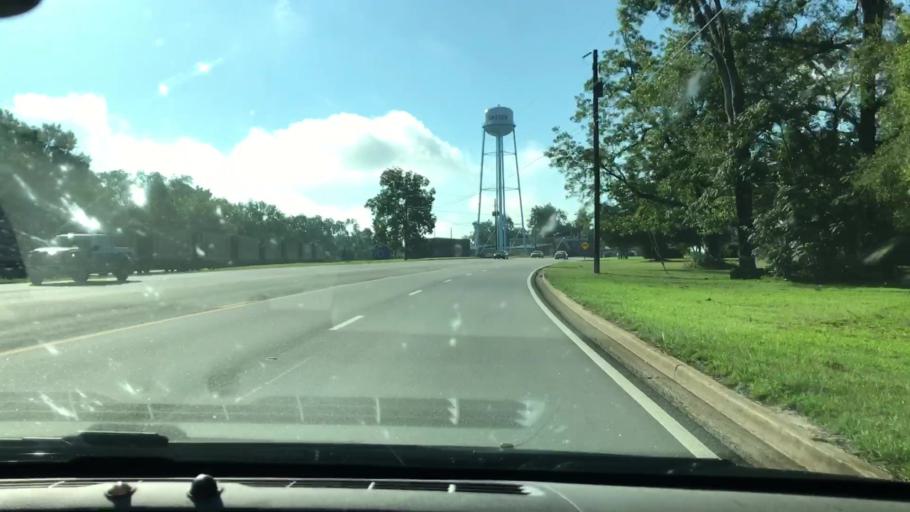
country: US
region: Georgia
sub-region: Terrell County
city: Dawson
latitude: 31.7216
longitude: -84.3506
